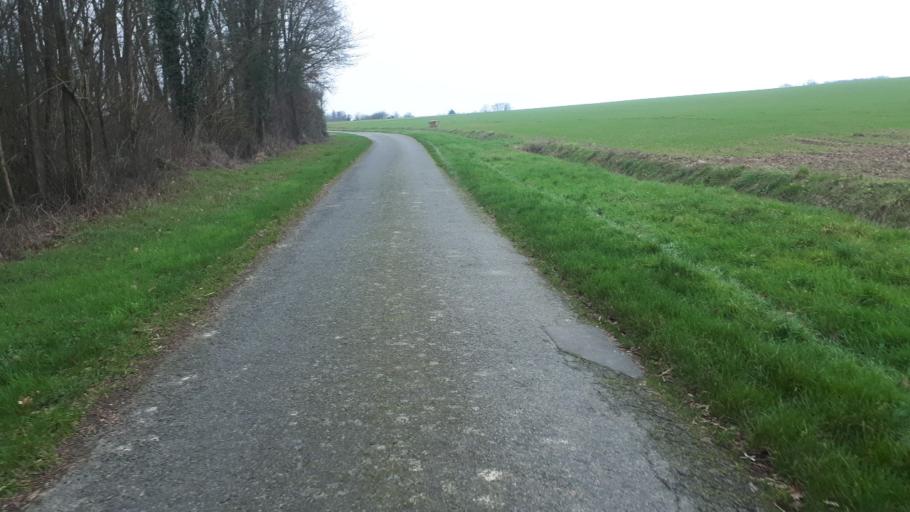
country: FR
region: Centre
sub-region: Departement du Loir-et-Cher
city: Villiers-sur-Loir
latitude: 47.8168
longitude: 0.9978
